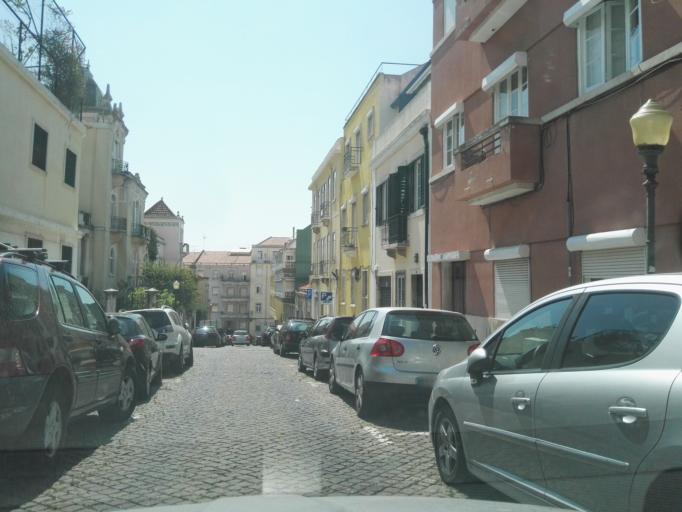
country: PT
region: Setubal
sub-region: Almada
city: Cacilhas
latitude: 38.7062
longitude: -9.1665
